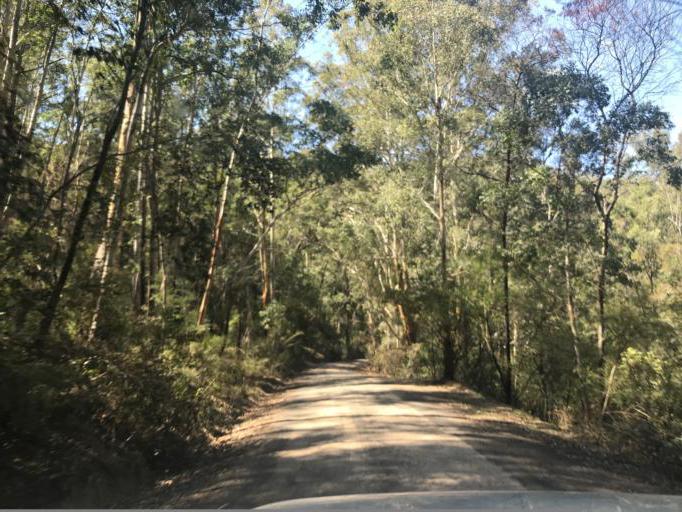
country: AU
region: New South Wales
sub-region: Wyong Shire
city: Little Jilliby
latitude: -33.1672
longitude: 151.0669
